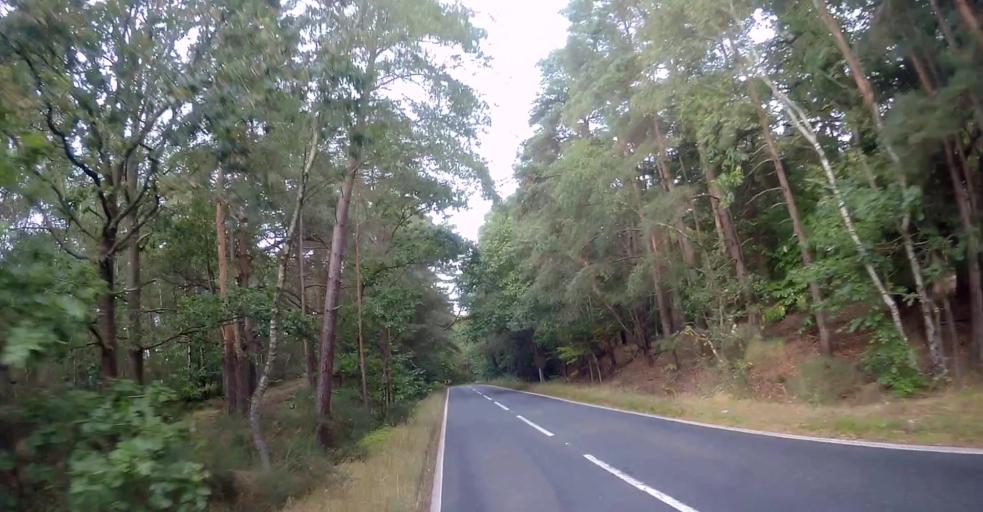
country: GB
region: England
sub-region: Surrey
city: Normandy
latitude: 51.2891
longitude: -0.6914
